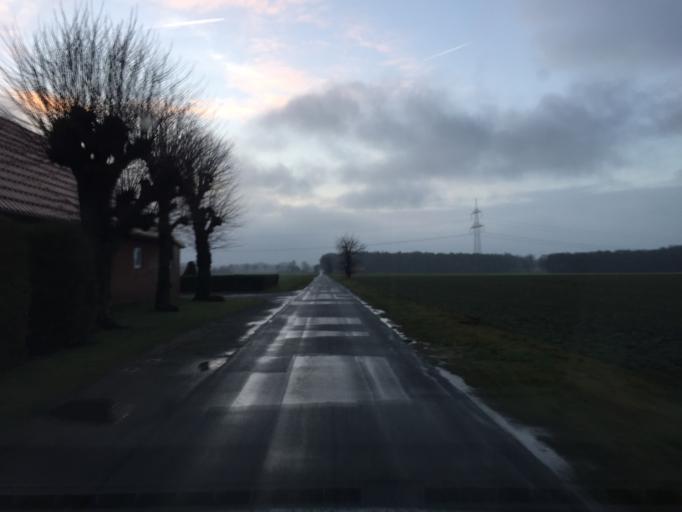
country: DE
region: Lower Saxony
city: Pennigsehl
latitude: 52.6588
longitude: 9.0235
